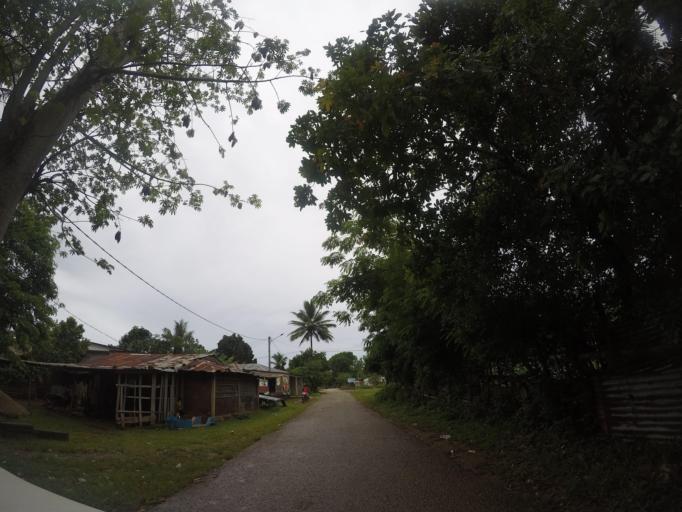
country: TL
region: Lautem
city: Lospalos
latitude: -8.5198
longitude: 127.0011
